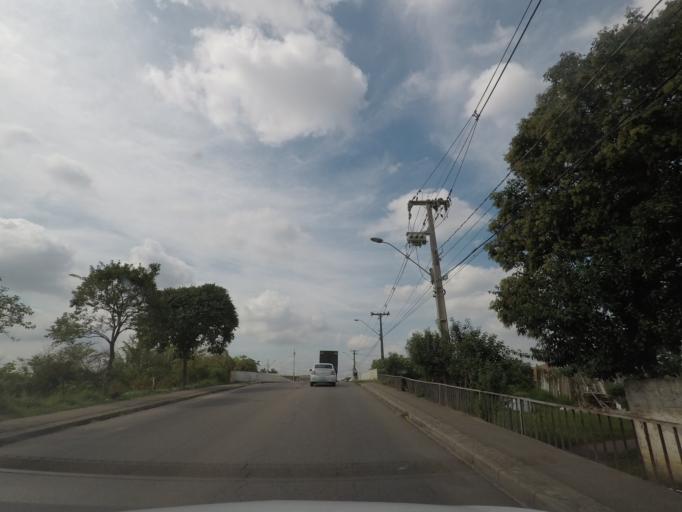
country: BR
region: Parana
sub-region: Pinhais
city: Pinhais
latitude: -25.4652
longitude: -49.1910
